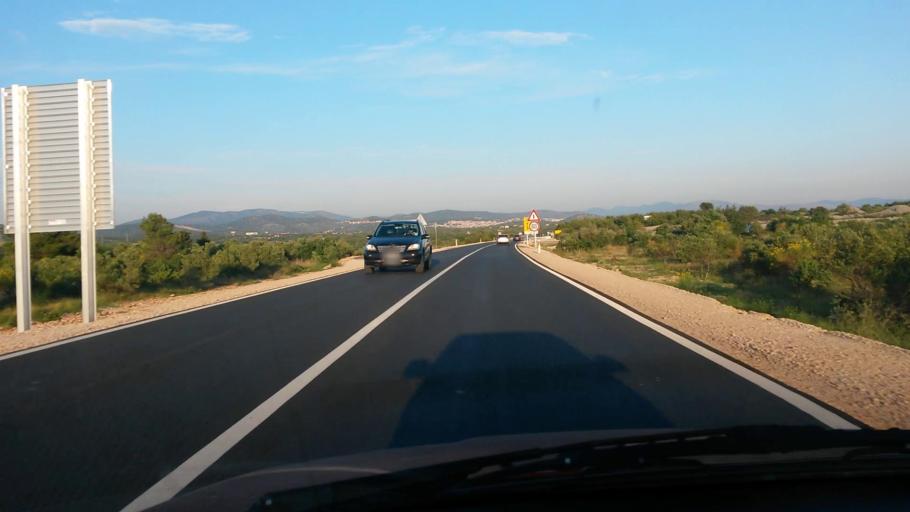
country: HR
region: Sibensko-Kniniska
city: Zaton
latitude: 43.7640
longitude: 15.8143
